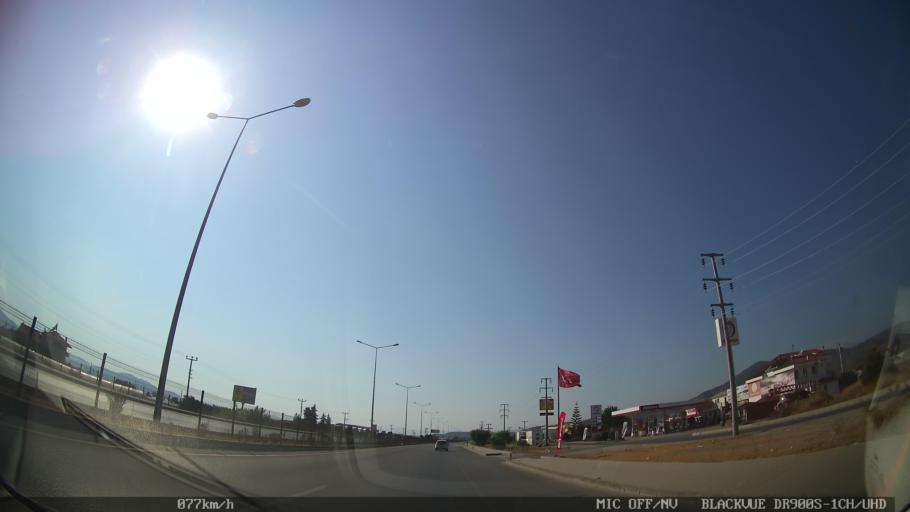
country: TR
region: Mugla
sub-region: Fethiye
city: Fethiye
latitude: 36.6561
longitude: 29.1616
